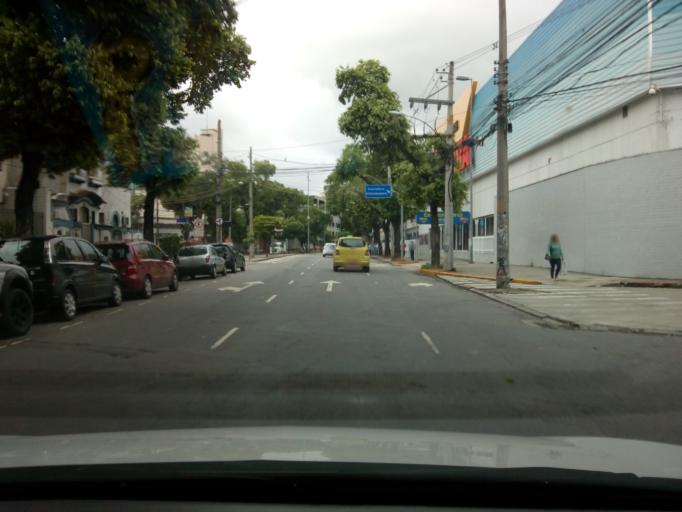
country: BR
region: Rio de Janeiro
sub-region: Rio De Janeiro
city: Rio de Janeiro
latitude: -22.9200
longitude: -43.2266
